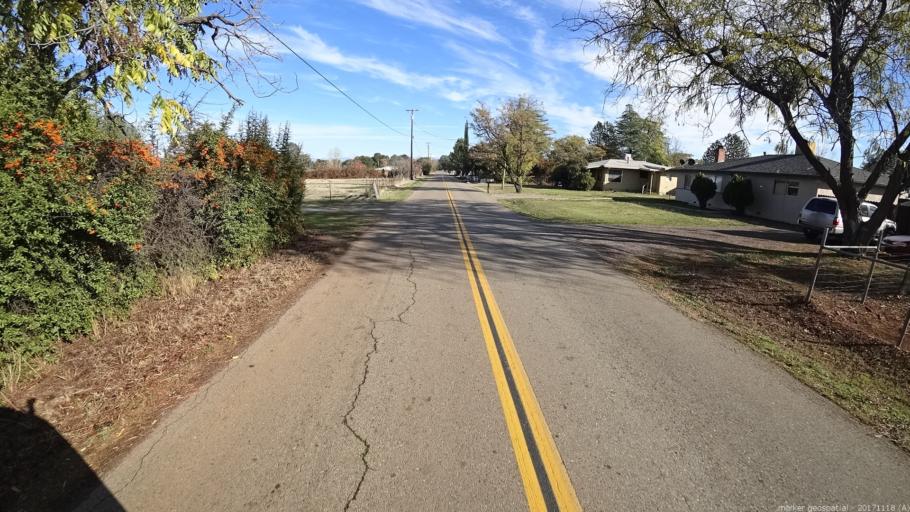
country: US
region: California
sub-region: Shasta County
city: Anderson
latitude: 40.4762
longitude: -122.3965
